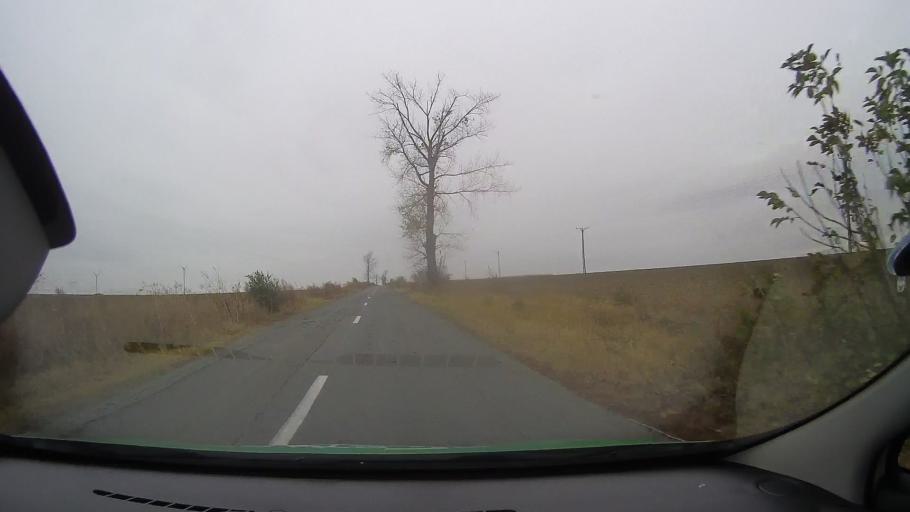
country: RO
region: Constanta
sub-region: Comuna Pantelimon
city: Pantelimon
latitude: 44.5607
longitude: 28.3217
